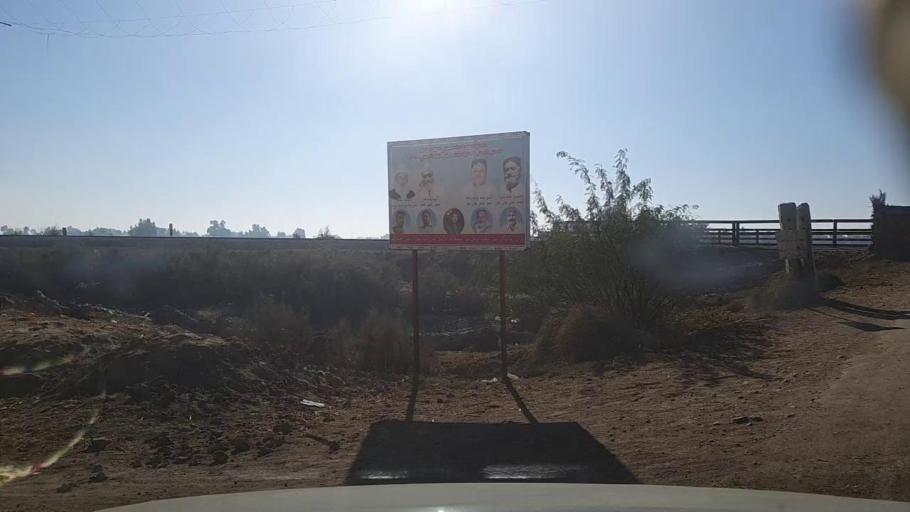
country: PK
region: Sindh
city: Khairpur
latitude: 28.0395
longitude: 69.6545
